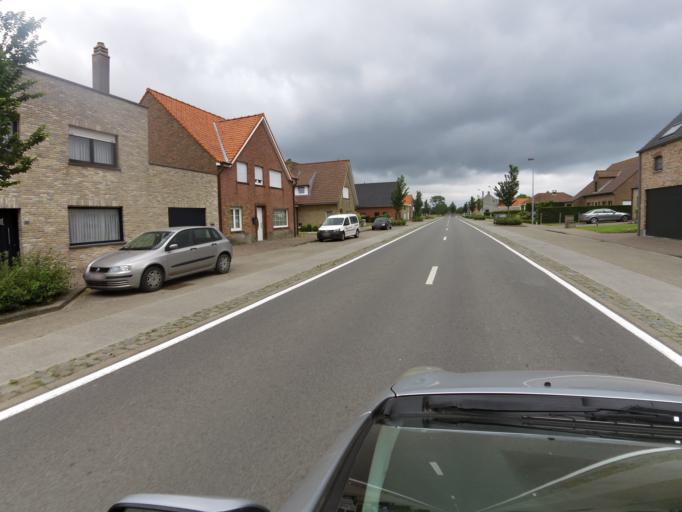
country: BE
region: Flanders
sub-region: Provincie West-Vlaanderen
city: Diksmuide
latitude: 51.0971
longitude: 2.8984
